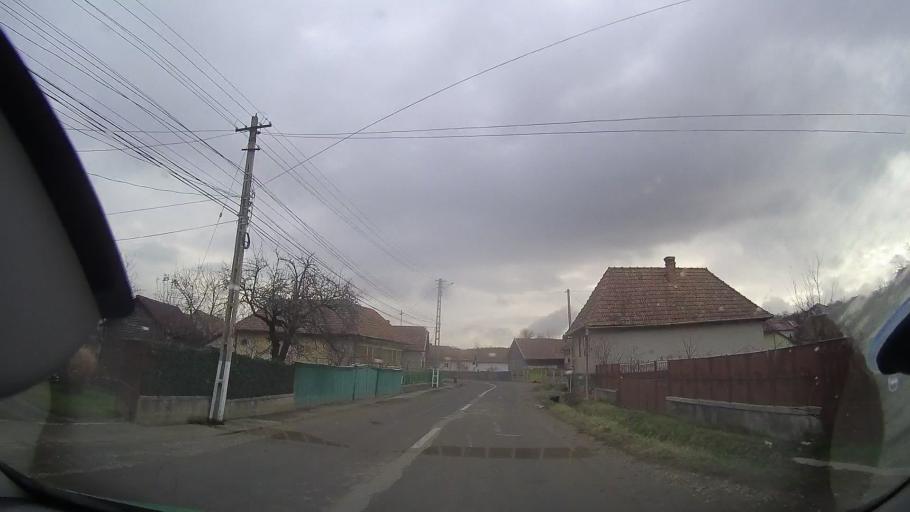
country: RO
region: Cluj
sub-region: Comuna Moldovenesti
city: Moldovenesti
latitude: 46.4998
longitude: 23.6676
